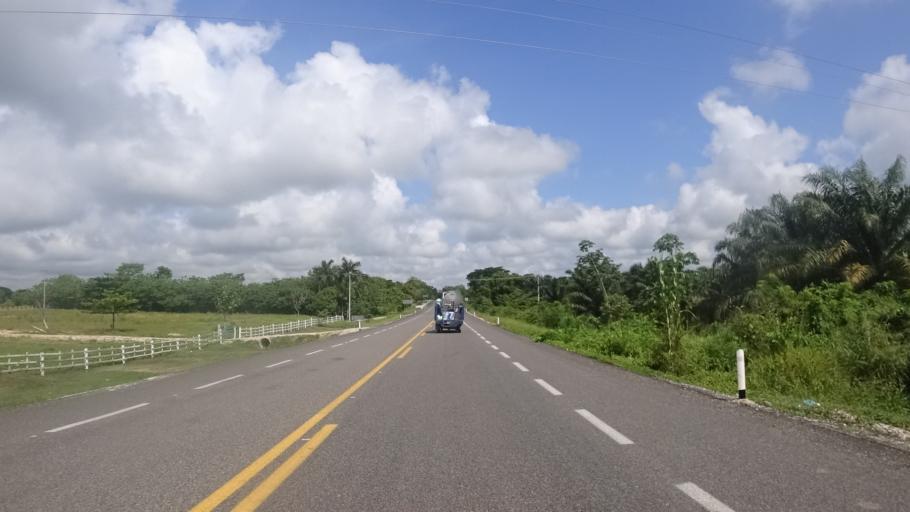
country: MX
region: Chiapas
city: Palenque
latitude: 17.5812
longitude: -92.0319
